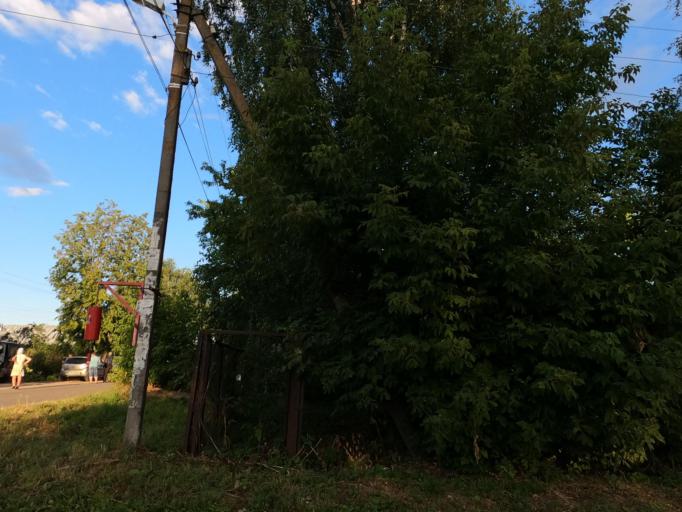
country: RU
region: Moskovskaya
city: Ashitkovo
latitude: 55.4205
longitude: 38.5730
